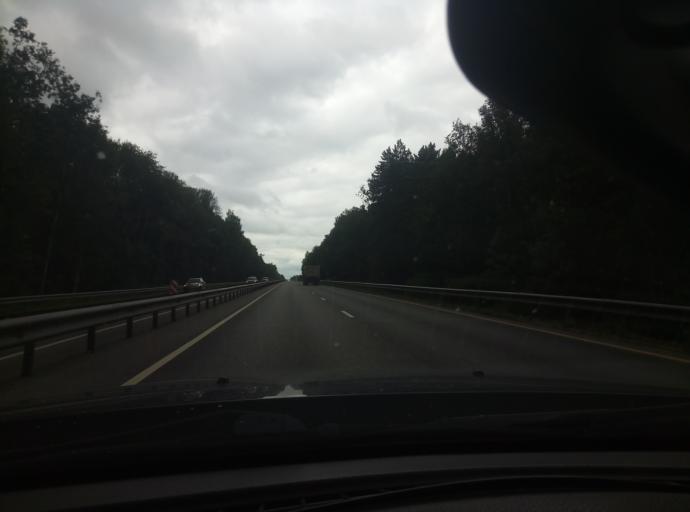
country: RU
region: Kaluga
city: Maloyaroslavets
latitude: 54.9884
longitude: 36.5083
